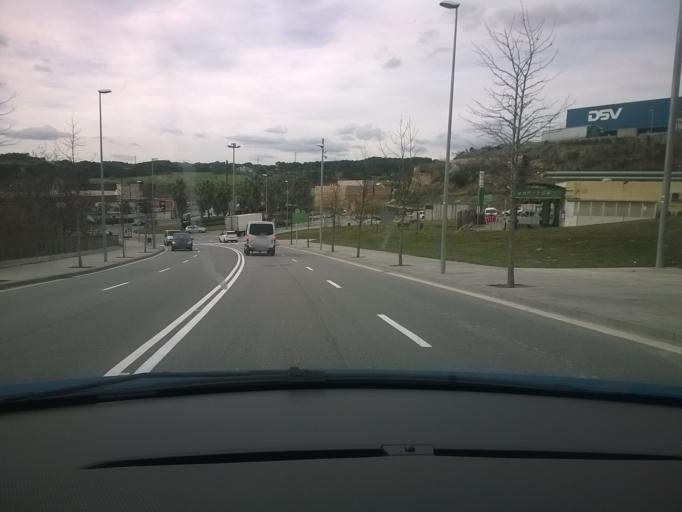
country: ES
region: Catalonia
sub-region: Provincia de Barcelona
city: Rubi
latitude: 41.5065
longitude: 2.0375
